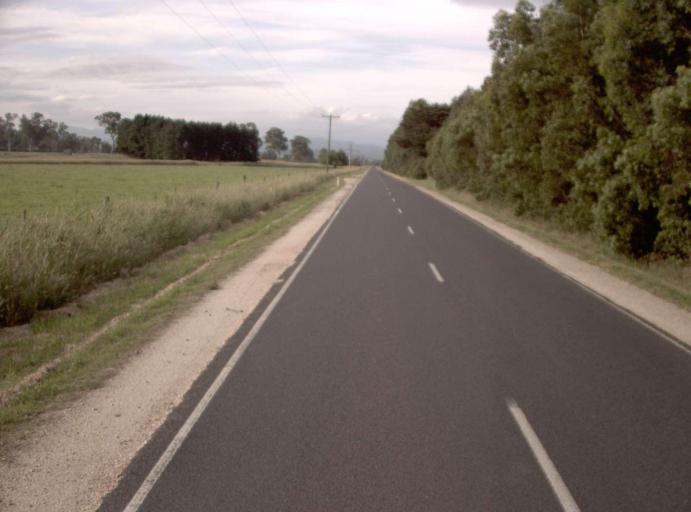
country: AU
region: Victoria
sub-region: Wellington
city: Sale
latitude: -37.9111
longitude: 146.9961
